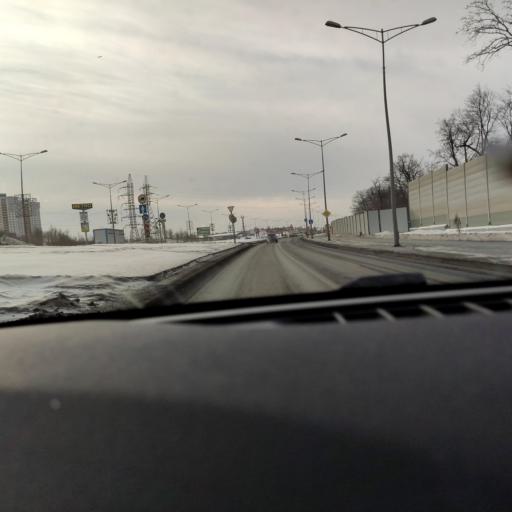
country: RU
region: Samara
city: Petra-Dubrava
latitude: 53.2835
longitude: 50.2809
